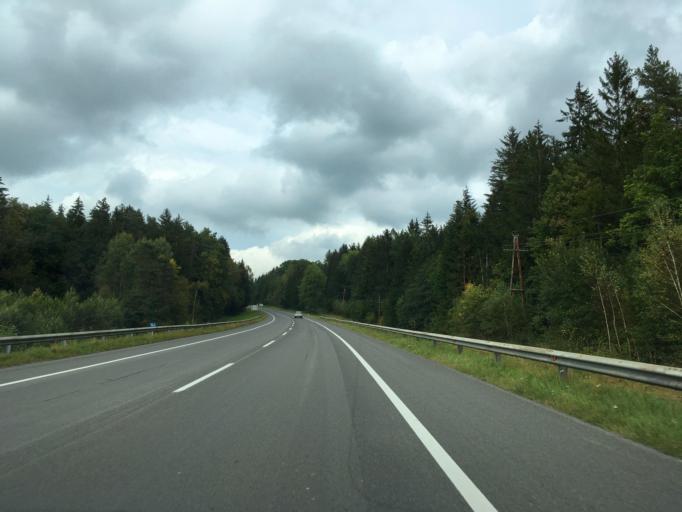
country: AT
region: Styria
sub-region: Politischer Bezirk Hartberg-Fuerstenfeld
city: Friedberg
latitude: 47.4209
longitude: 16.0527
